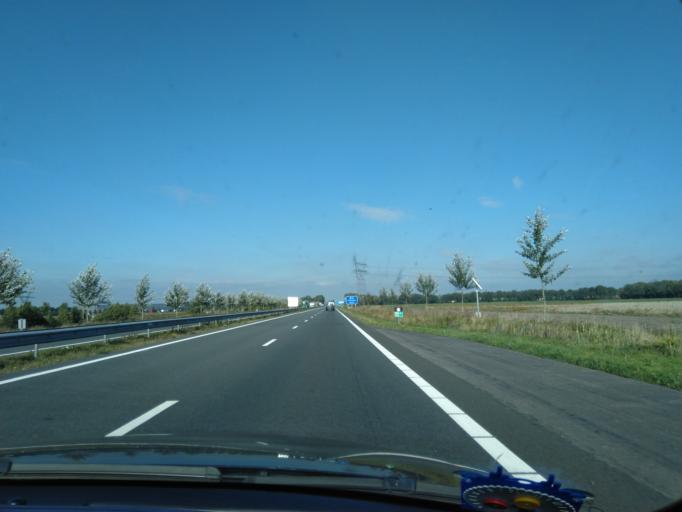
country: NL
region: Groningen
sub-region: Gemeente Veendam
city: Veendam
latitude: 53.0838
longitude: 6.8860
